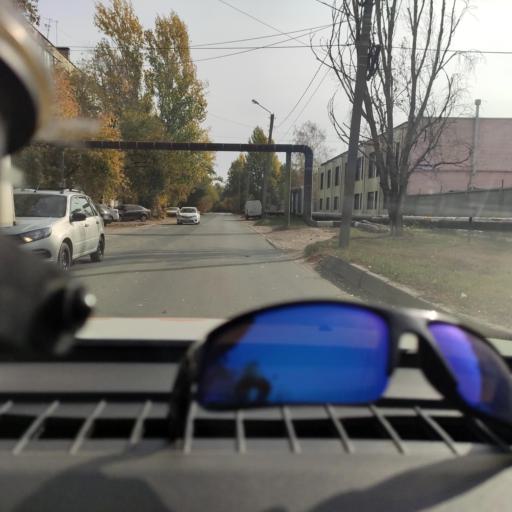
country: RU
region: Samara
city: Samara
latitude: 53.1198
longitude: 50.0872
